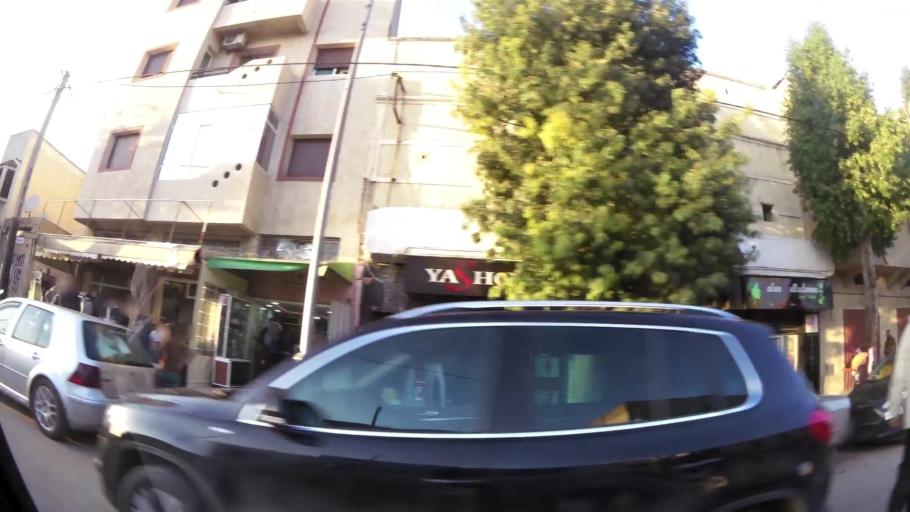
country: MA
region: Chaouia-Ouardigha
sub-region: Settat Province
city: Settat
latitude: 33.0004
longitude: -7.6178
